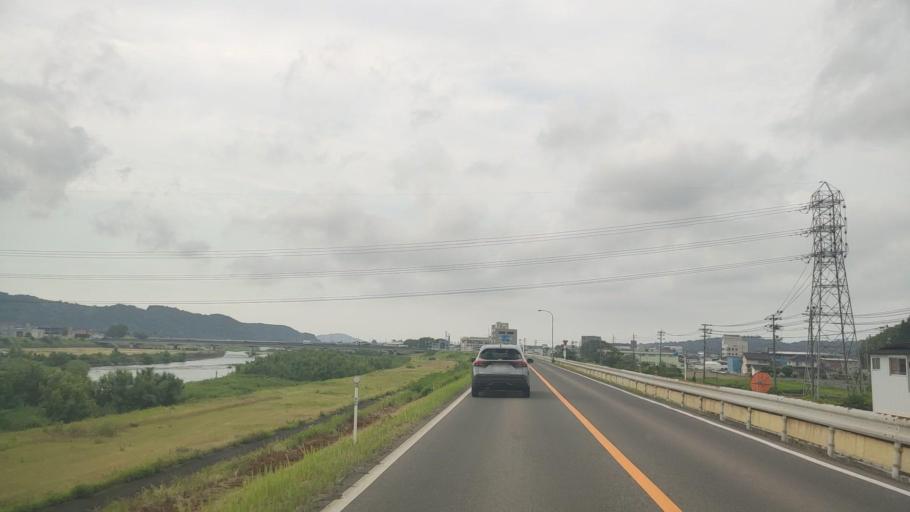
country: JP
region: Tottori
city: Kurayoshi
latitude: 35.4367
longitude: 133.8481
